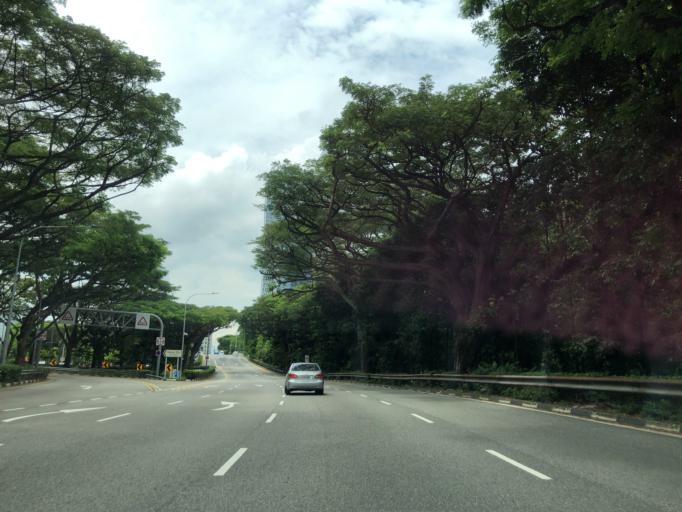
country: SG
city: Singapore
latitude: 1.2956
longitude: 103.8606
